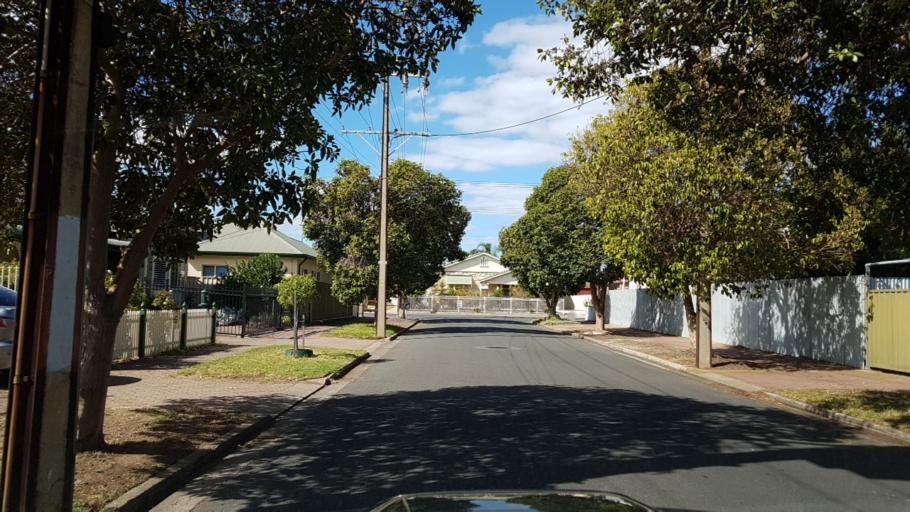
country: AU
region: South Australia
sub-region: Holdfast Bay
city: Glenelg East
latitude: -34.9727
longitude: 138.5217
